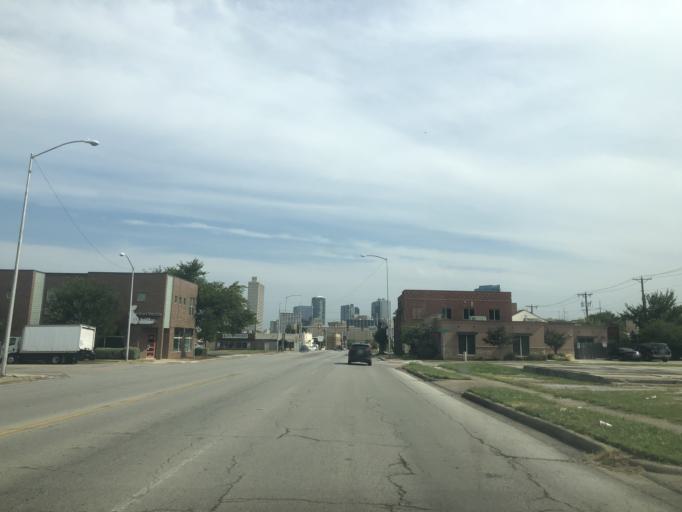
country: US
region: Texas
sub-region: Tarrant County
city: Fort Worth
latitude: 32.7368
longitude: -97.3318
